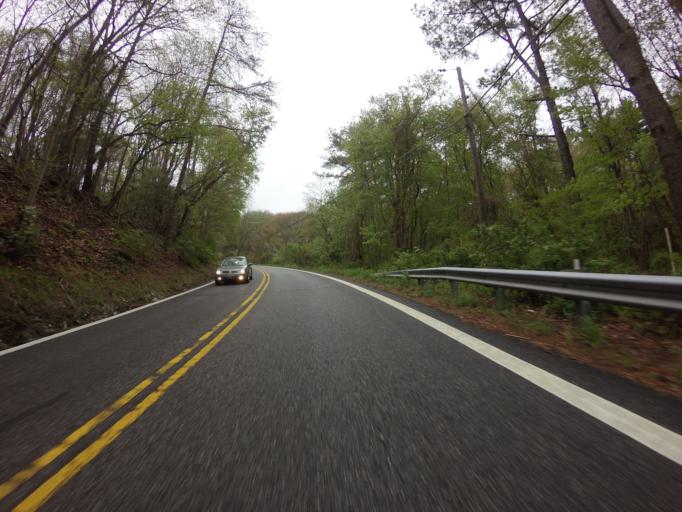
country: US
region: Maryland
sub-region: Carroll County
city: Hampstead
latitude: 39.5751
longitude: -76.7588
